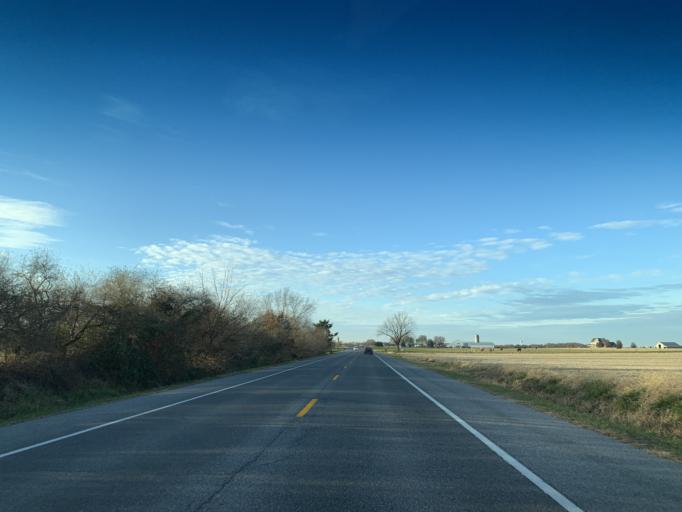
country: US
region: Maryland
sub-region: Kent County
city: Chestertown
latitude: 39.2556
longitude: -76.0807
